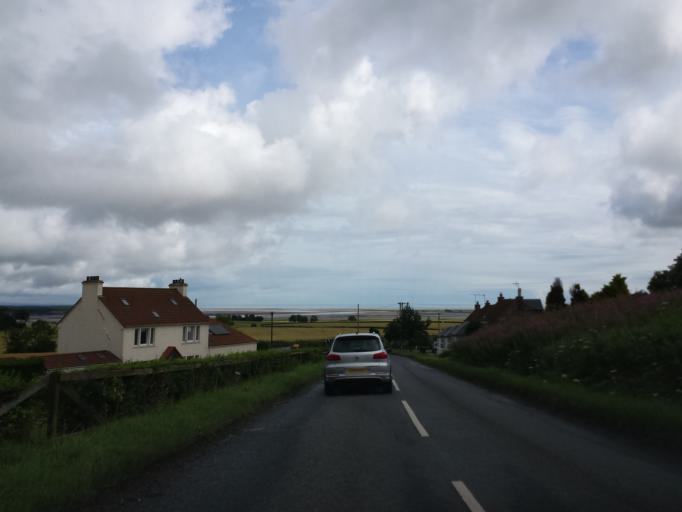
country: GB
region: Scotland
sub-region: Fife
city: Strathkinness
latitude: 56.3467
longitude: -2.8719
